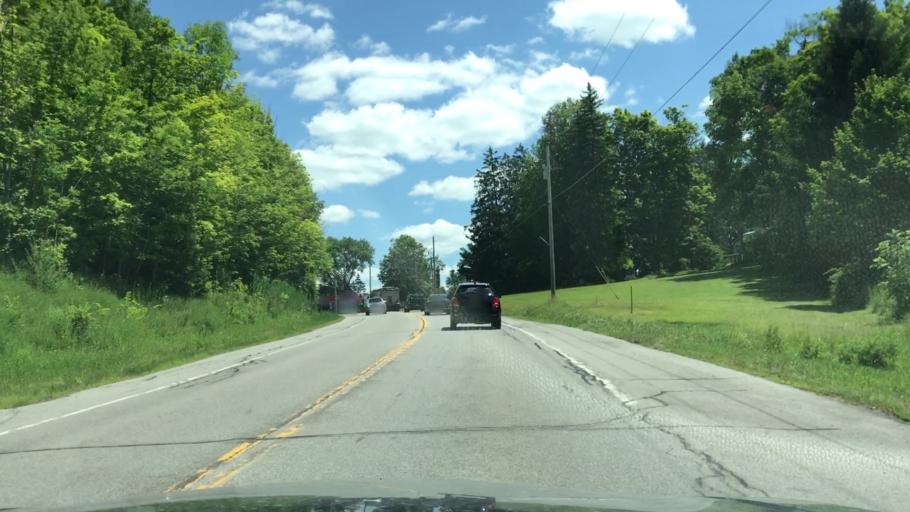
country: US
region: New York
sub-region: Wyoming County
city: Attica
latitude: 42.7591
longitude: -78.3108
